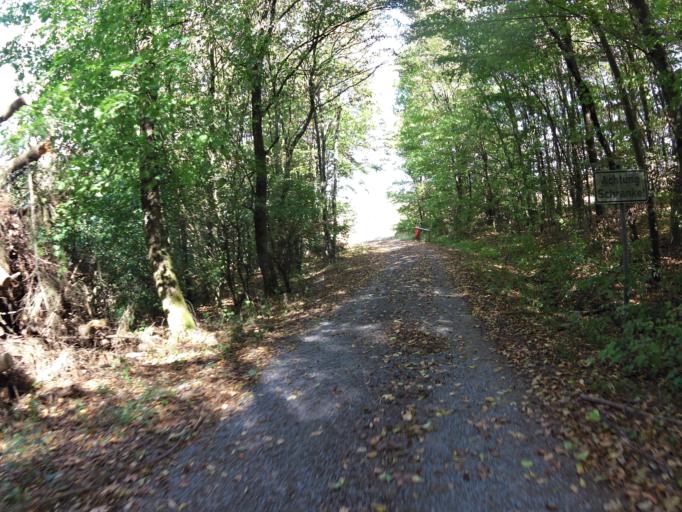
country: DE
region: Bavaria
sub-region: Regierungsbezirk Unterfranken
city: Eisingen
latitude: 49.7732
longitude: 9.8334
